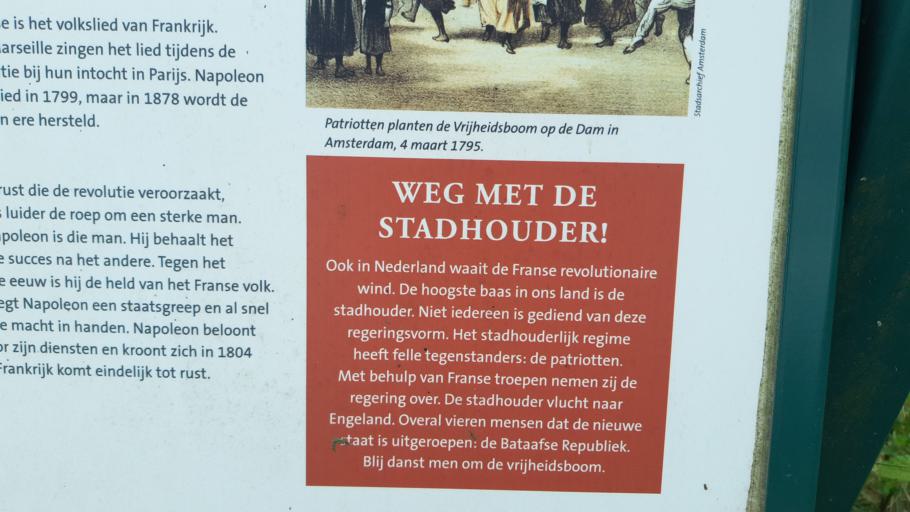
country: NL
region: Gelderland
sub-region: Gemeente Lochem
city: Laren
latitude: 52.2934
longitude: 6.3945
